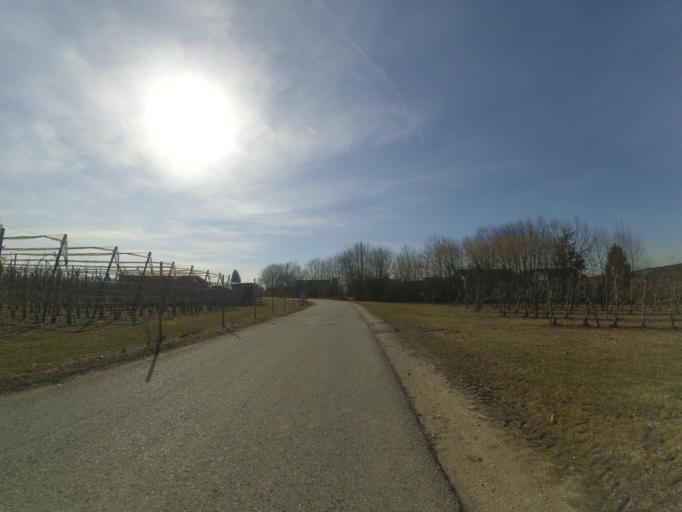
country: DE
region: Baden-Wuerttemberg
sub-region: Tuebingen Region
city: Meckenbeuren
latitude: 47.7075
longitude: 9.5630
